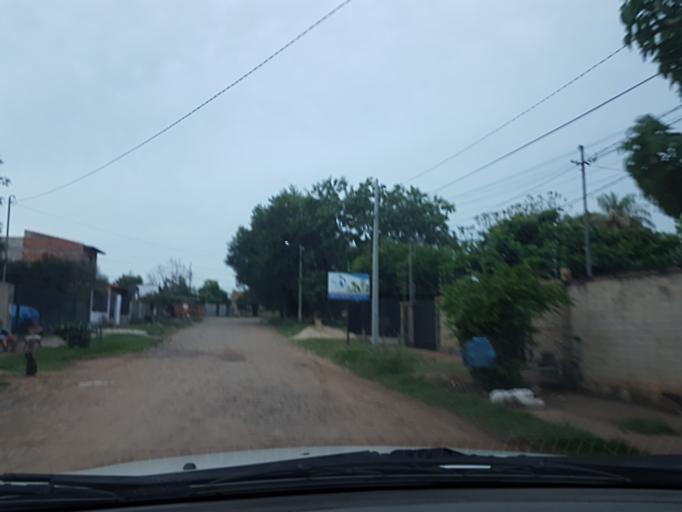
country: PY
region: Central
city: Colonia Mariano Roque Alonso
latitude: -25.2368
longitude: -57.5366
